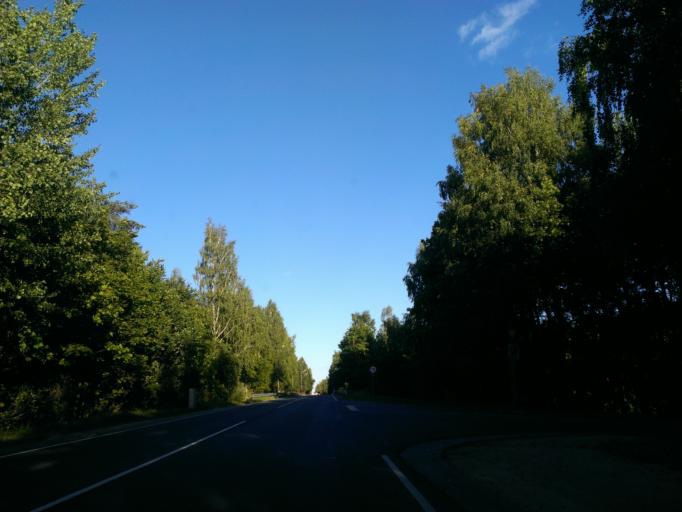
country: LV
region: Riga
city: Bergi
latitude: 57.0026
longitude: 24.2698
